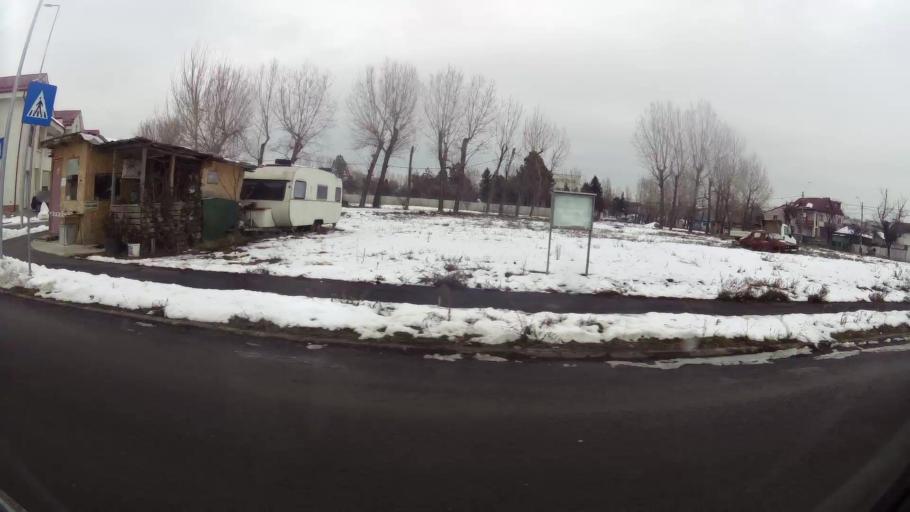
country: RO
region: Bucuresti
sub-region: Municipiul Bucuresti
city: Bucuresti
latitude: 44.4116
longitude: 26.0545
